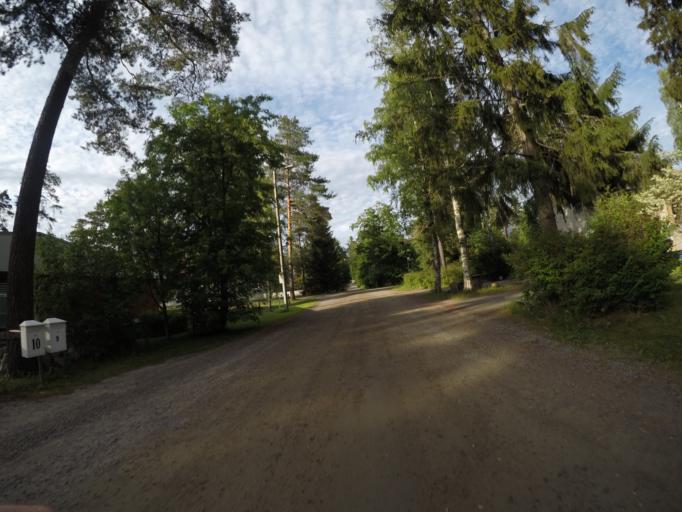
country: FI
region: Haeme
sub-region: Haemeenlinna
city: Haemeenlinna
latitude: 60.9792
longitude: 24.4092
